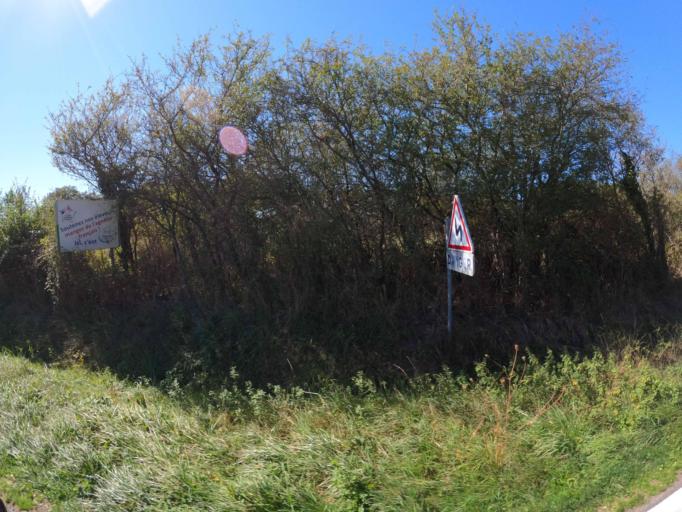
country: FR
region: Poitou-Charentes
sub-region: Departement de la Vienne
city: Lathus-Saint-Remy
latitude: 46.3044
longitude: 0.9874
